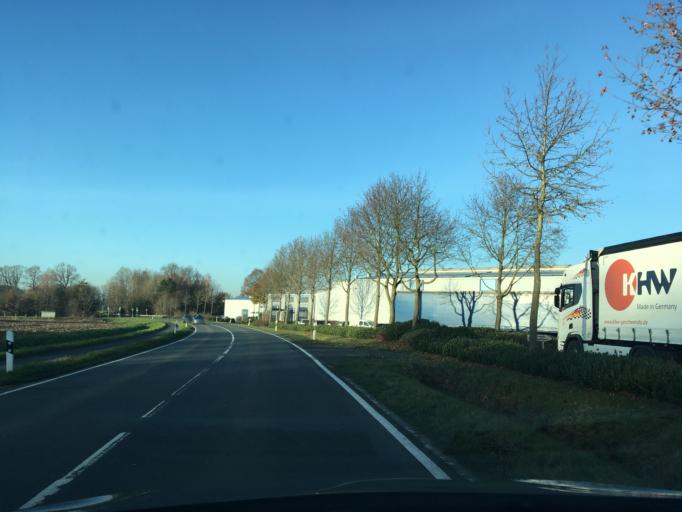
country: DE
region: North Rhine-Westphalia
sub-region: Regierungsbezirk Munster
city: Ahaus
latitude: 52.1058
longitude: 6.9630
